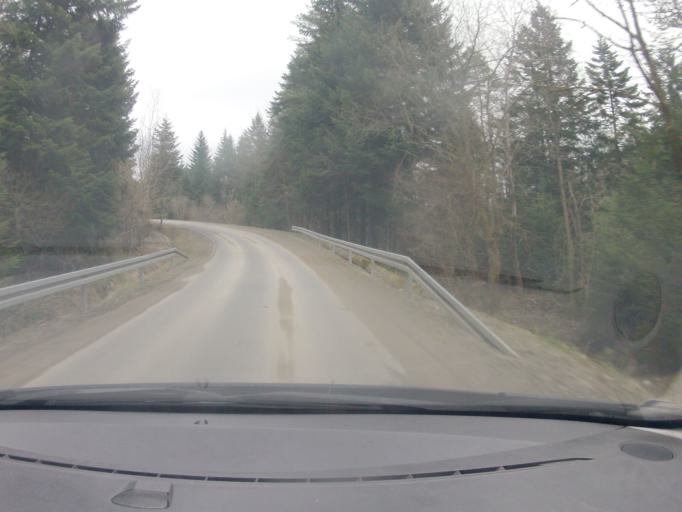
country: PL
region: Subcarpathian Voivodeship
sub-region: Powiat krosnienski
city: Dukla
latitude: 49.5009
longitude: 21.6200
